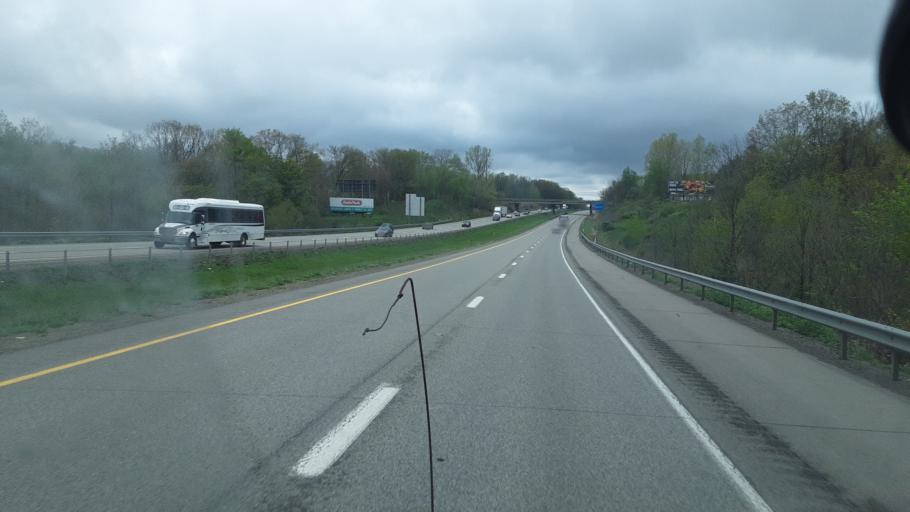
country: US
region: Pennsylvania
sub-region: Erie County
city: Wesleyville
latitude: 42.1023
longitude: -79.9889
